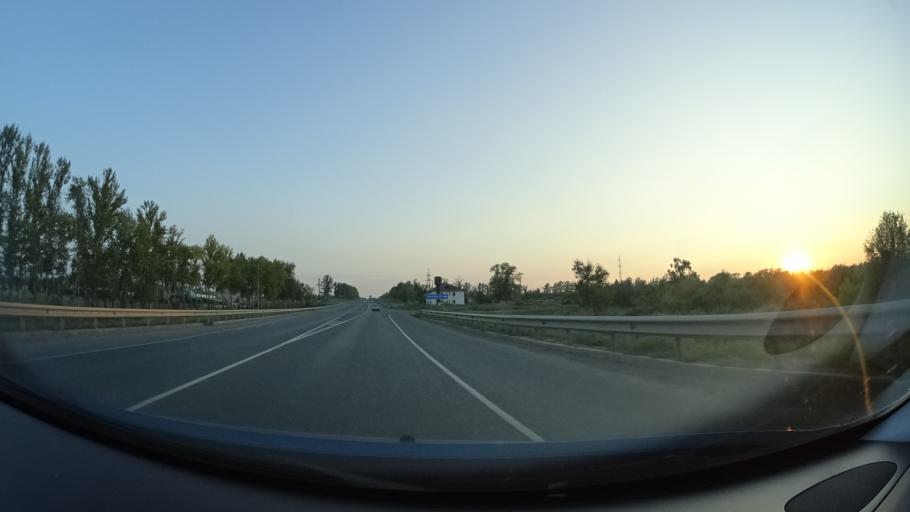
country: RU
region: Samara
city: Sukhodol
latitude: 53.8845
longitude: 51.2419
